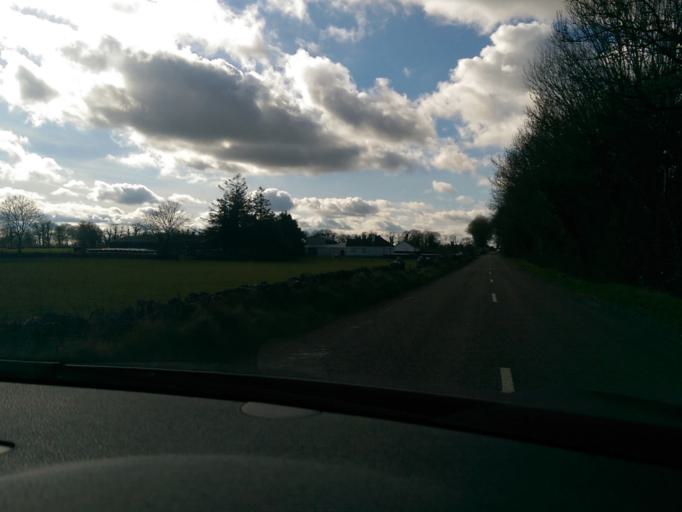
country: IE
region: Connaught
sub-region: Roscommon
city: Castlerea
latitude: 53.5137
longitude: -8.5739
